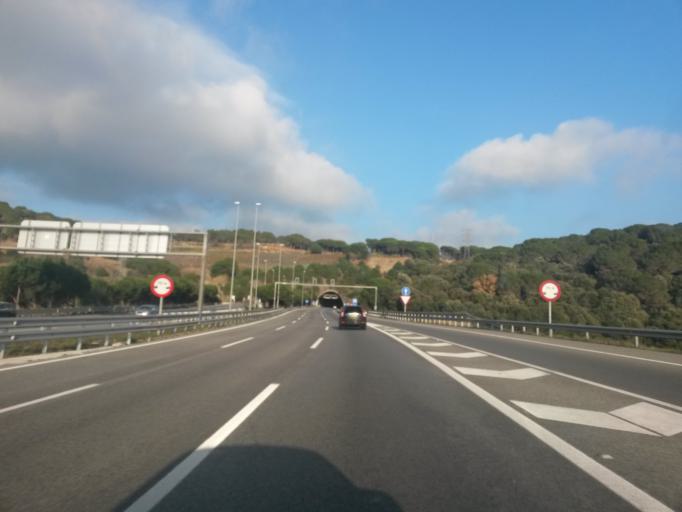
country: ES
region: Catalonia
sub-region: Provincia de Barcelona
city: Canet de Mar
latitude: 41.5962
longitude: 2.5722
